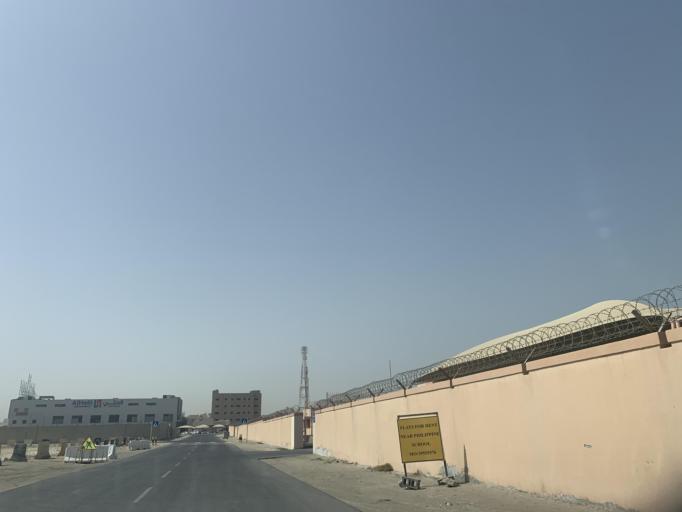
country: BH
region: Northern
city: Madinat `Isa
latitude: 26.1557
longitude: 50.5271
